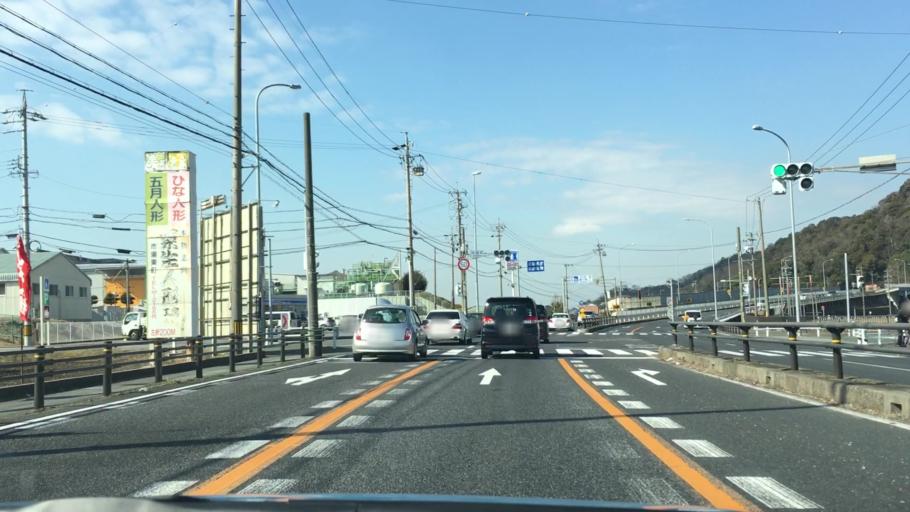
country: JP
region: Aichi
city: Gamagori
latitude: 34.9070
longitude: 137.2312
